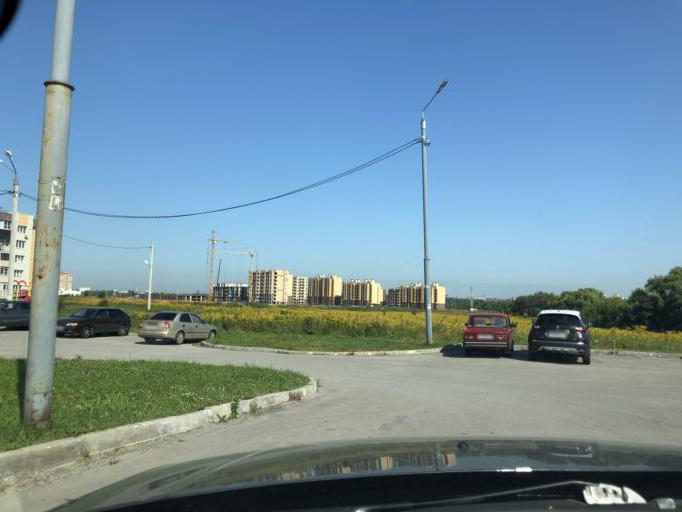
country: RU
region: Tula
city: Tula
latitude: 54.1758
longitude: 37.6572
